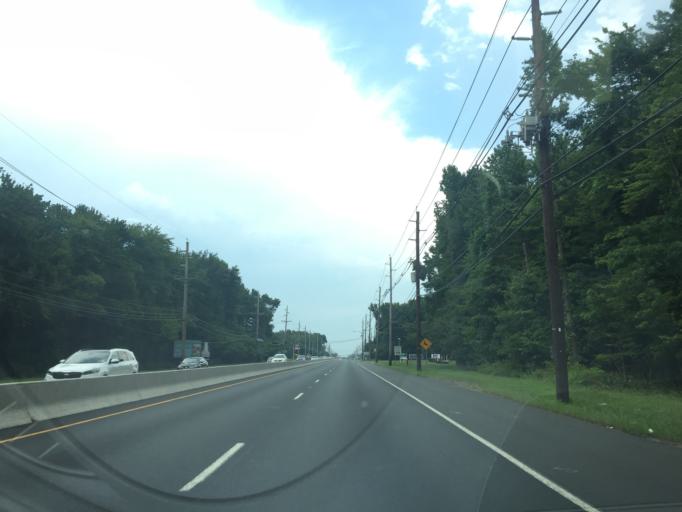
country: US
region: New Jersey
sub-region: Middlesex County
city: Kendall Park
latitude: 40.4331
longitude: -74.5142
